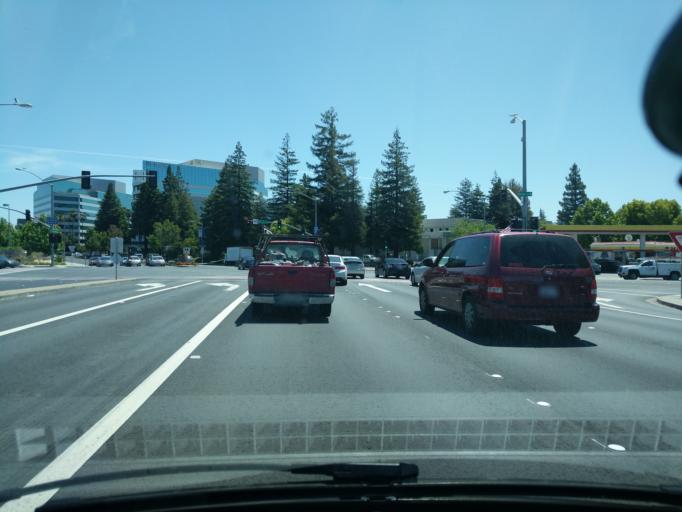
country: US
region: California
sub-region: Contra Costa County
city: Concord
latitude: 37.9710
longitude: -122.0466
